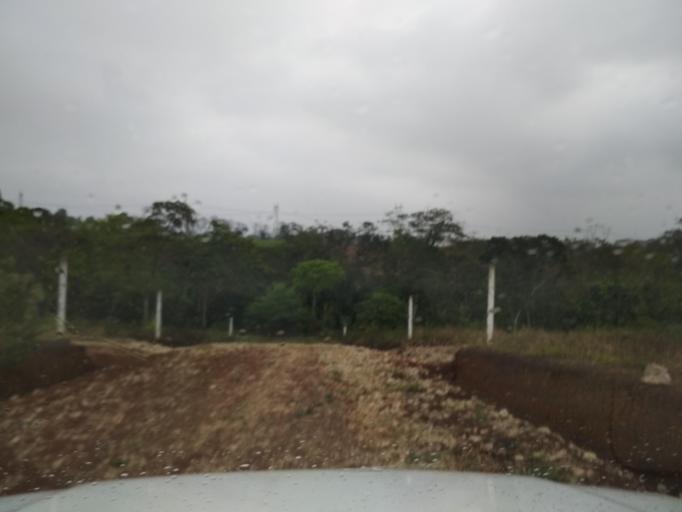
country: MX
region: Veracruz
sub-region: Cordoba
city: San Jose de Tapia
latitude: 18.8538
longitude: -96.9571
